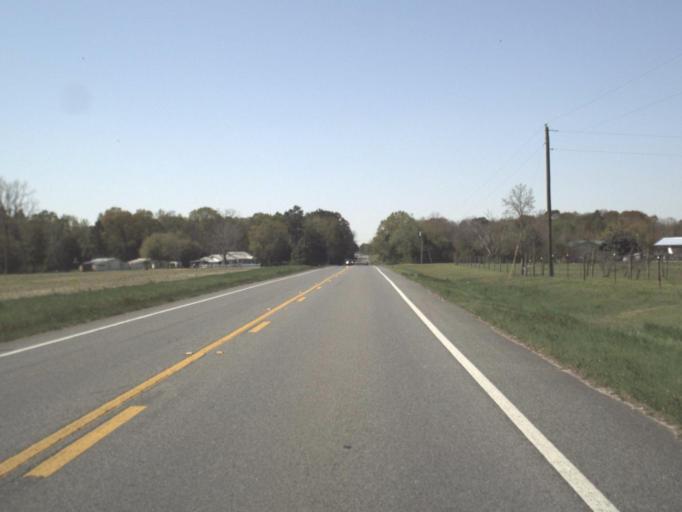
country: US
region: Florida
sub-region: Jackson County
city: Graceville
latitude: 30.8864
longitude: -85.4706
